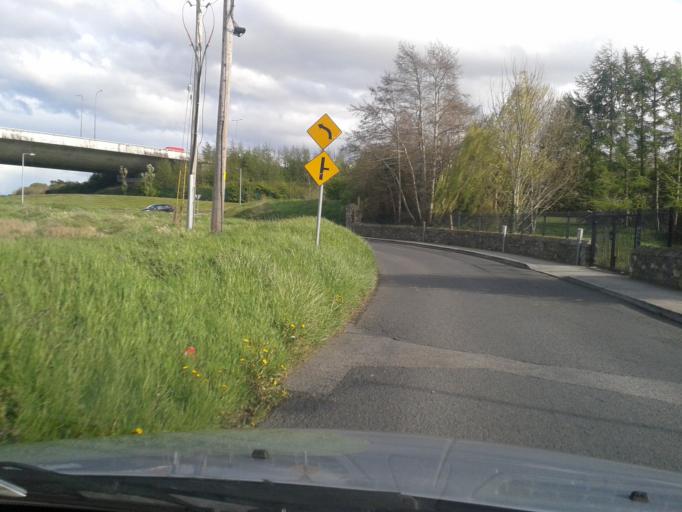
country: IE
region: Leinster
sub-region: Fingal County
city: Swords
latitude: 53.4651
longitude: -6.2054
